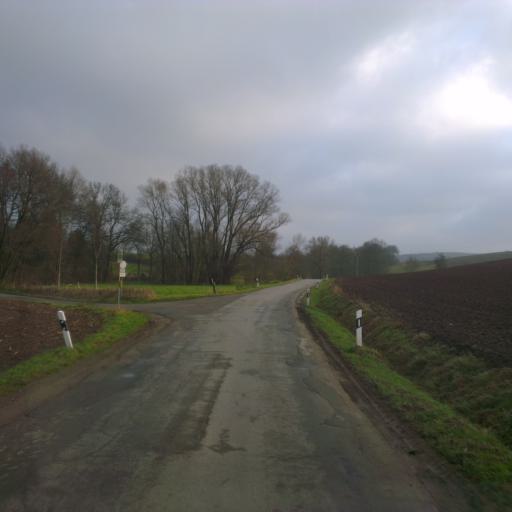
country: DE
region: Thuringia
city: Altenberga
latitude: 50.8329
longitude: 11.5485
